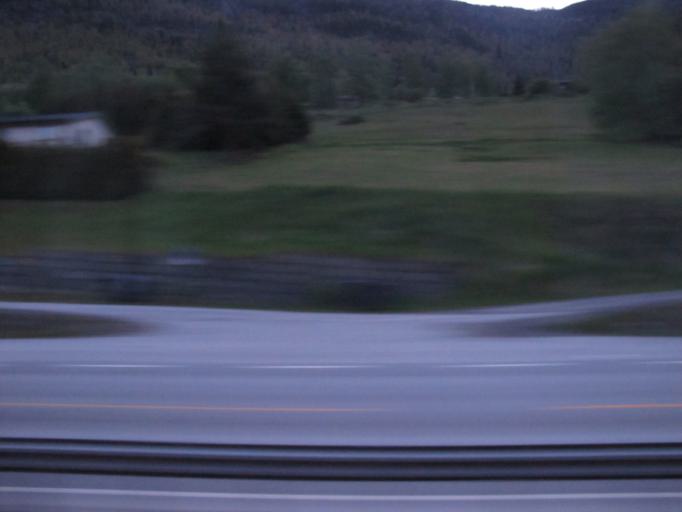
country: NO
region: Oppland
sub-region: Nord-Fron
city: Vinstra
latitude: 61.6656
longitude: 9.7196
